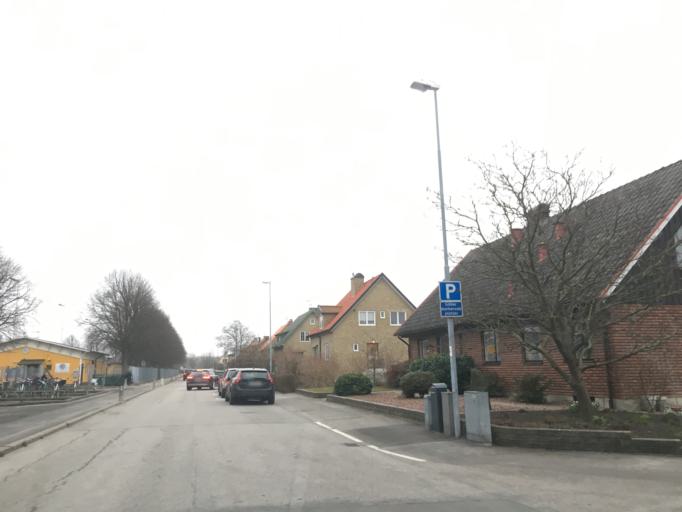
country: SE
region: Skane
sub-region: Lomma Kommun
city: Lomma
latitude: 55.6671
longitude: 13.0676
